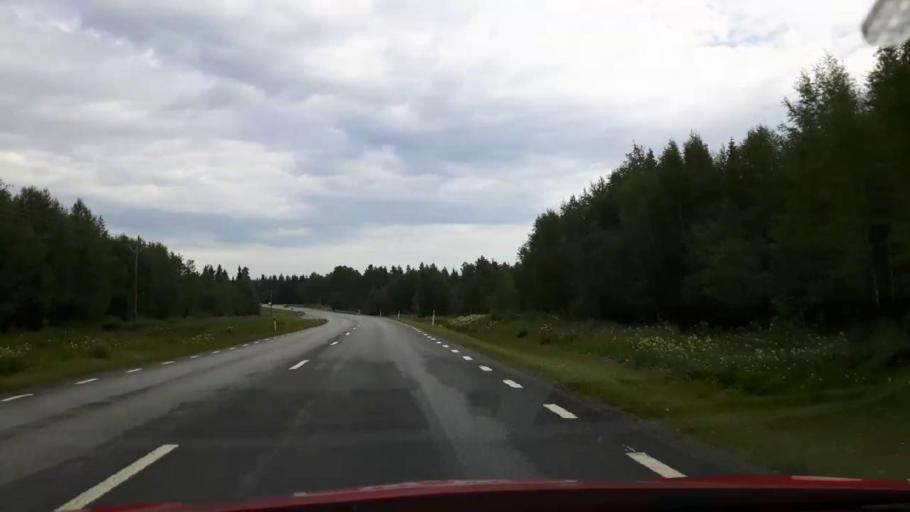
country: SE
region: Jaemtland
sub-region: Stroemsunds Kommun
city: Stroemsund
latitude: 63.6490
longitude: 15.3792
